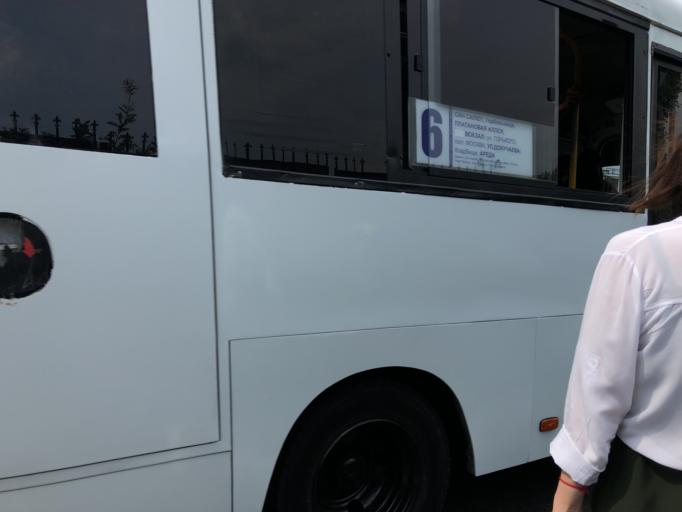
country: RU
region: Krasnodarskiy
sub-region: Sochi City
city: Sochi
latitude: 43.5942
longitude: 39.7419
